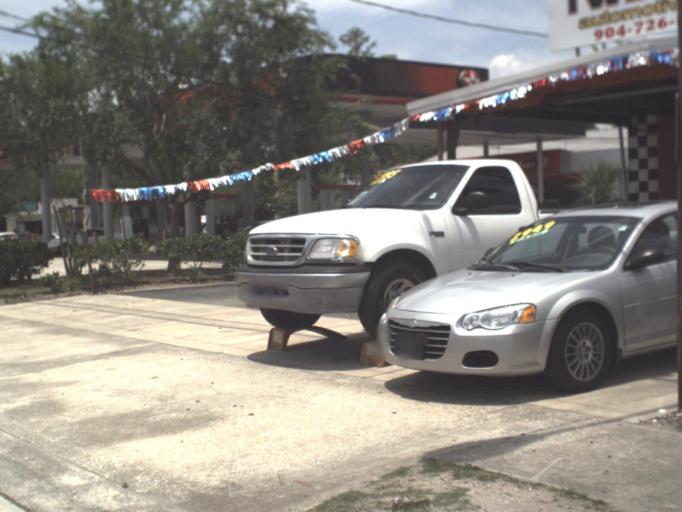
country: US
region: Florida
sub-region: Duval County
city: Jacksonville
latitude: 30.3141
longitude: -81.5683
